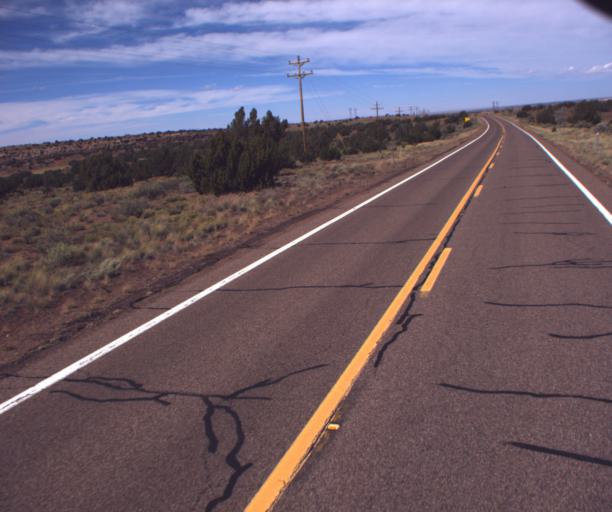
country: US
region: Arizona
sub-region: Apache County
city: Saint Johns
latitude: 34.5310
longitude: -109.6202
